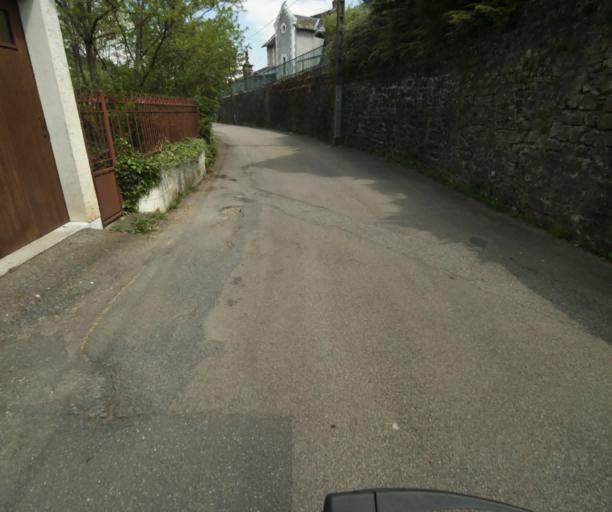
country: FR
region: Limousin
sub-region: Departement de la Correze
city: Tulle
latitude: 45.2732
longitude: 1.7726
